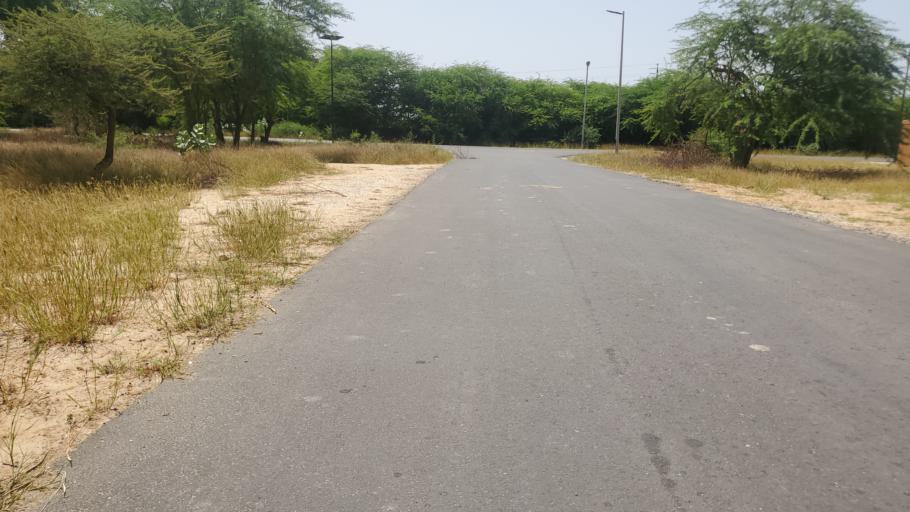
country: SN
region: Saint-Louis
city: Saint-Louis
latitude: 16.0582
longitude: -16.4271
